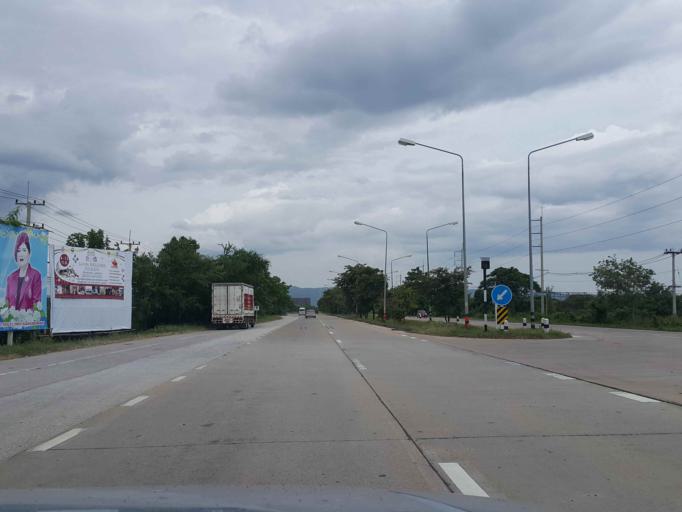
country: TH
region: Lampang
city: Lampang
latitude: 18.2912
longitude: 99.4293
